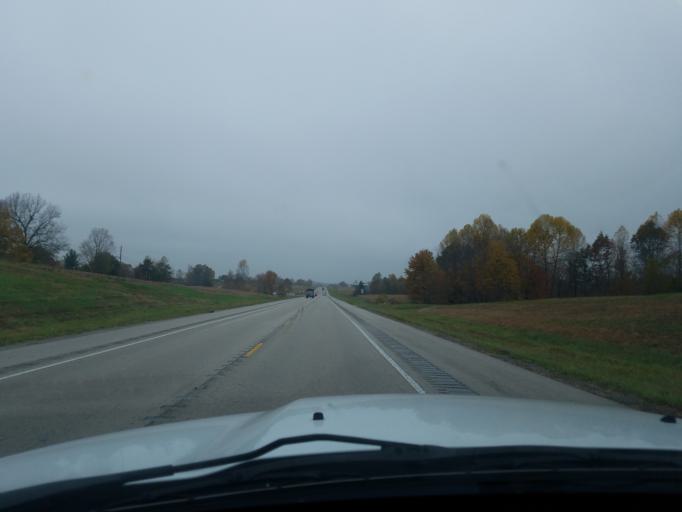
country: US
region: Kentucky
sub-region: Green County
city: Greensburg
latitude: 37.4125
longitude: -85.4912
